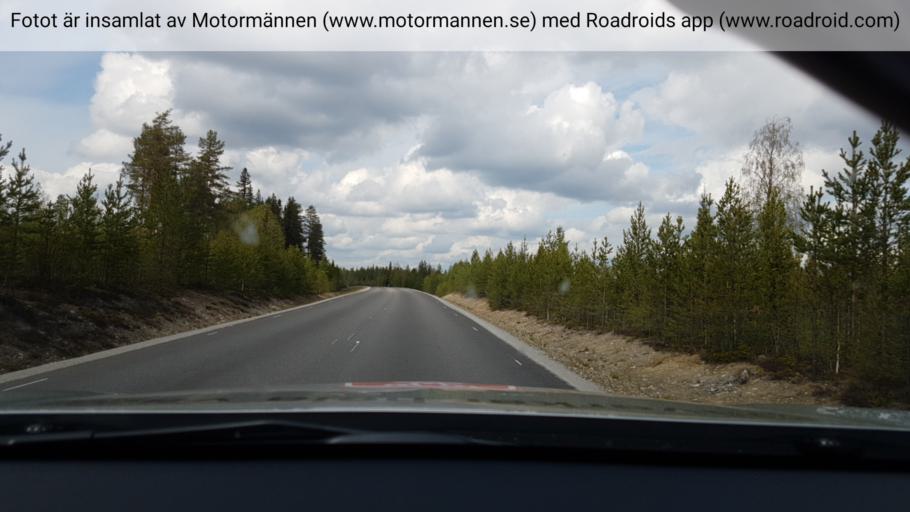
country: SE
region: Vaesterbotten
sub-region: Lycksele Kommun
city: Lycksele
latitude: 63.9835
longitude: 18.4844
